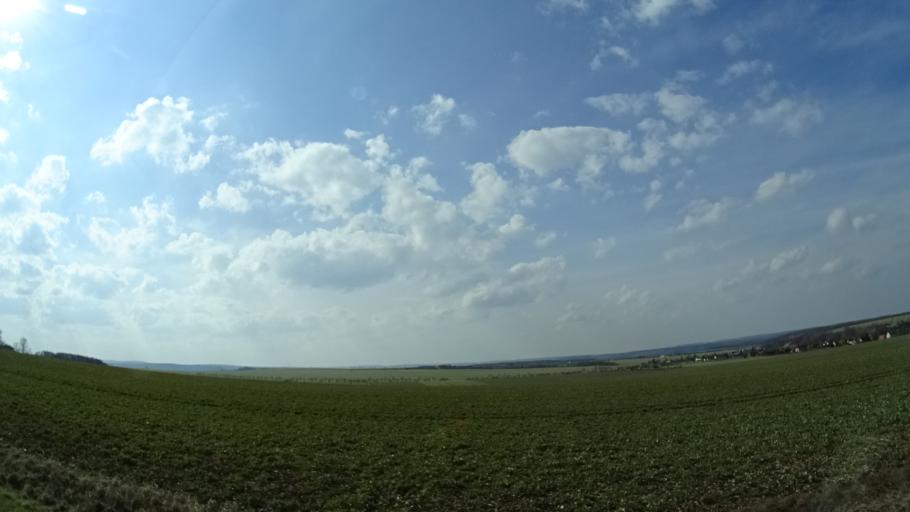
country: DE
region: Saxony-Anhalt
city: Prittitz
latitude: 51.1441
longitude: 11.9281
